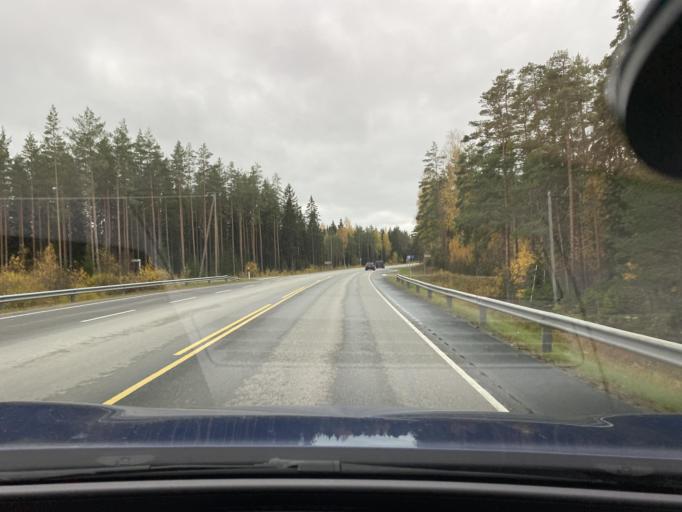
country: FI
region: Satakunta
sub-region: Rauma
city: Lappi
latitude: 61.1108
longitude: 21.9224
